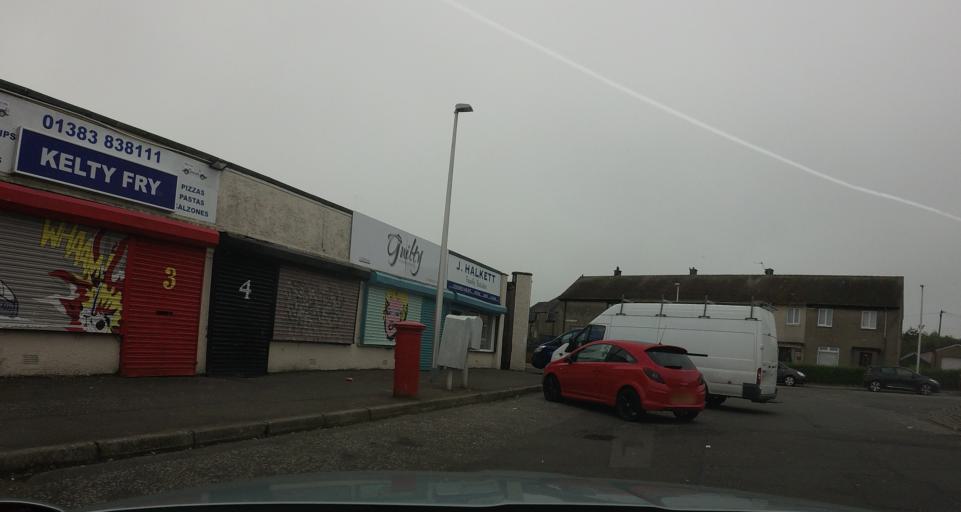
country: GB
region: Scotland
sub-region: Fife
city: Kelty
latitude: 56.1326
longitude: -3.3890
